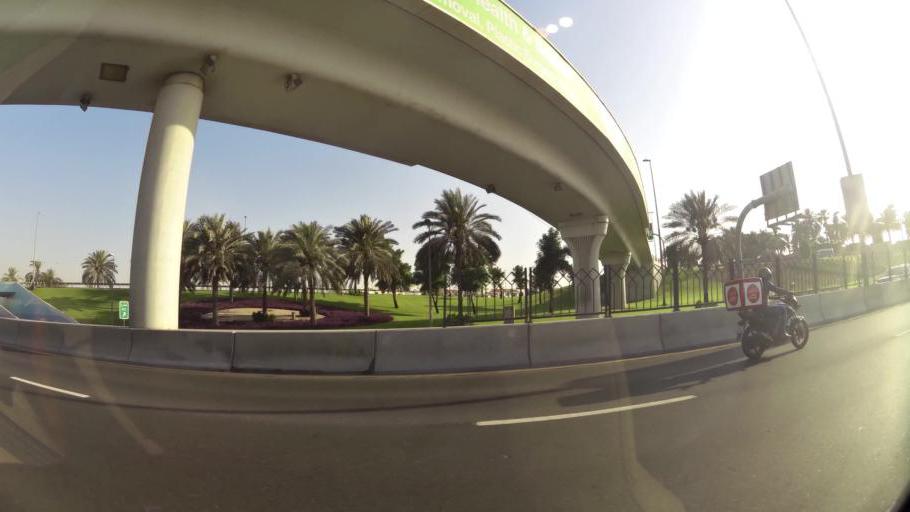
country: AE
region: Ash Shariqah
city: Sharjah
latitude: 25.2458
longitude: 55.3560
